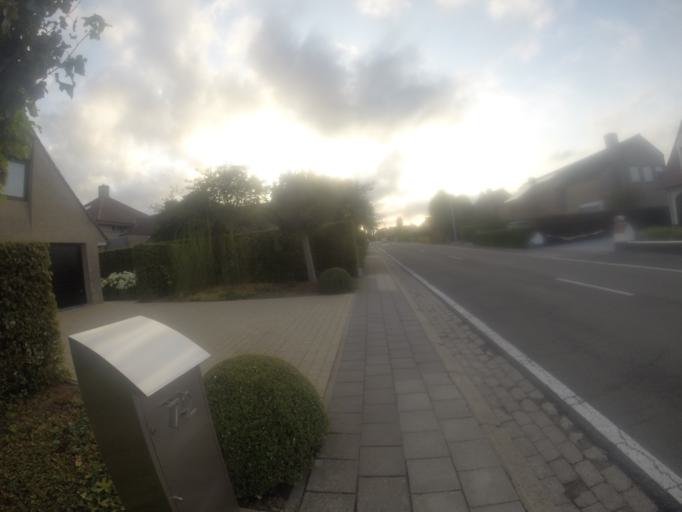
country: BE
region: Flanders
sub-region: Provincie West-Vlaanderen
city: Poperinge
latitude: 50.8617
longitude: 2.7261
